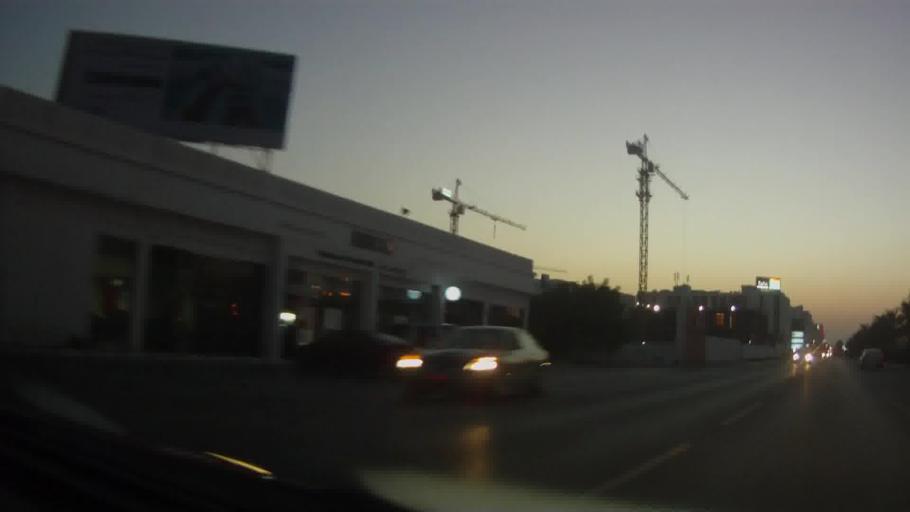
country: OM
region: Muhafazat Masqat
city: Bawshar
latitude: 23.5969
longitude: 58.4357
